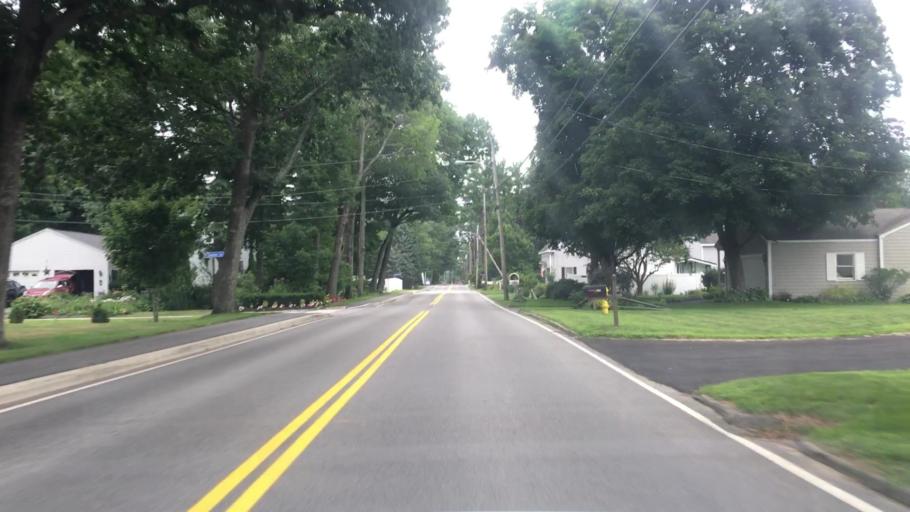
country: US
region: Maine
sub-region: York County
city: Biddeford
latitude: 43.5126
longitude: -70.4673
